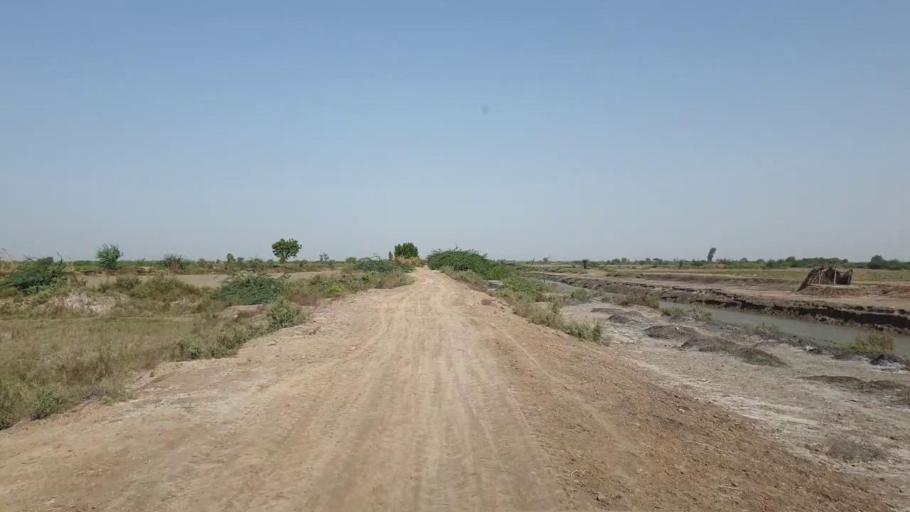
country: PK
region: Sindh
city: Tando Bago
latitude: 24.7016
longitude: 69.0707
